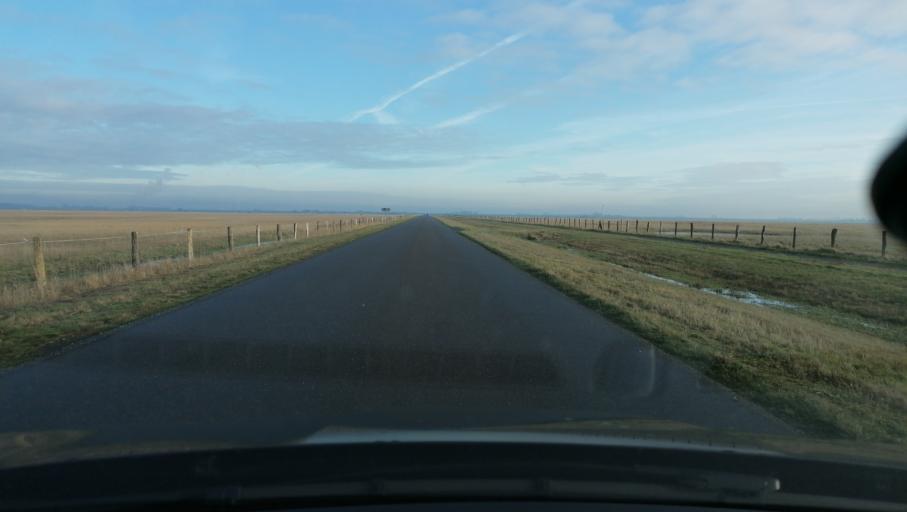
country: DE
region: Schleswig-Holstein
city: Friedrichsgabekoog
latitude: 54.1165
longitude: 8.9524
